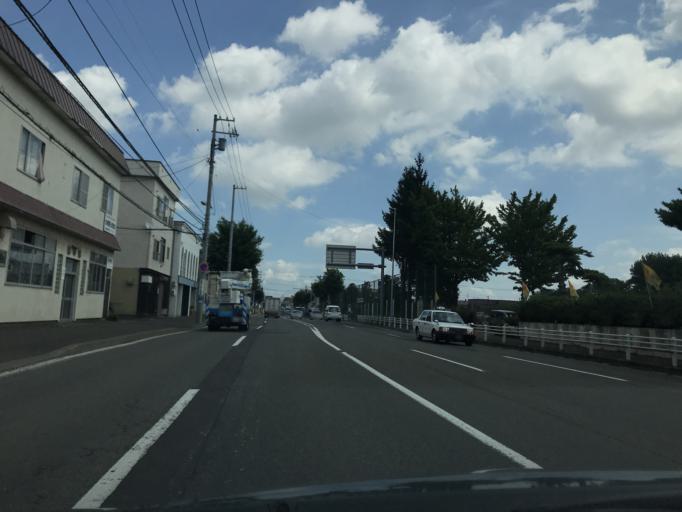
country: JP
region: Hokkaido
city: Sapporo
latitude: 43.0623
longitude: 141.3862
